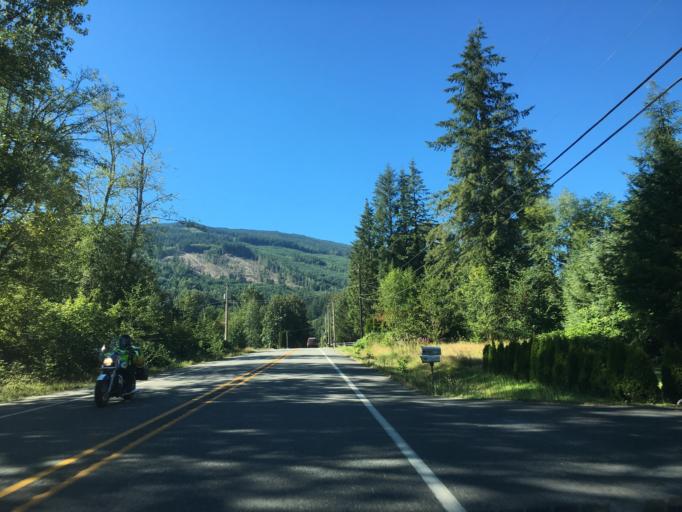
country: US
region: Washington
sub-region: Skagit County
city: Sedro-Woolley
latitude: 48.5973
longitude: -122.2303
